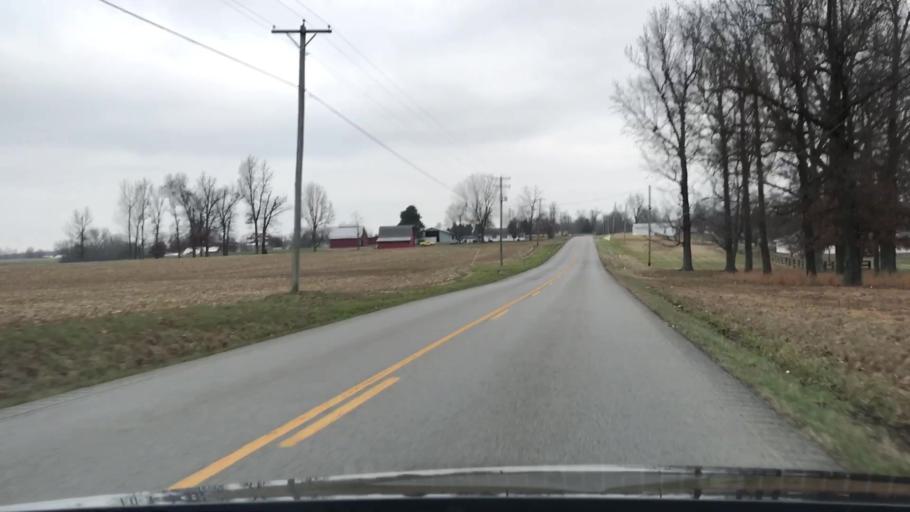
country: US
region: Kentucky
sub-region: McLean County
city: Calhoun
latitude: 37.3951
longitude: -87.2568
